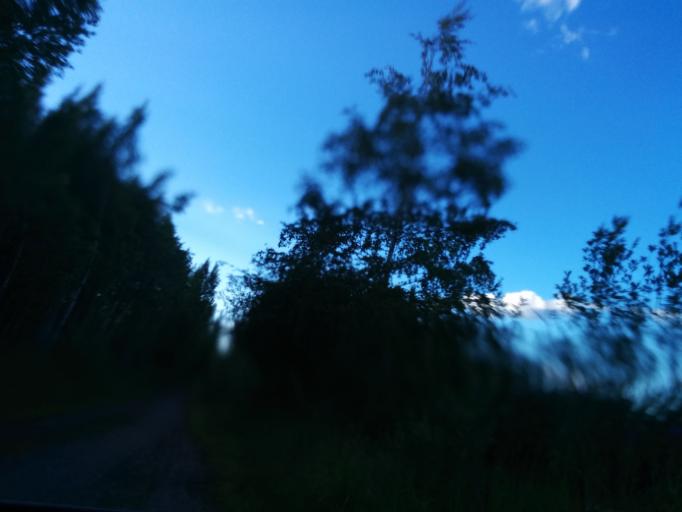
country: FI
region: Uusimaa
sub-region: Helsinki
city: Helsinki
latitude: 60.1999
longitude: 24.9790
